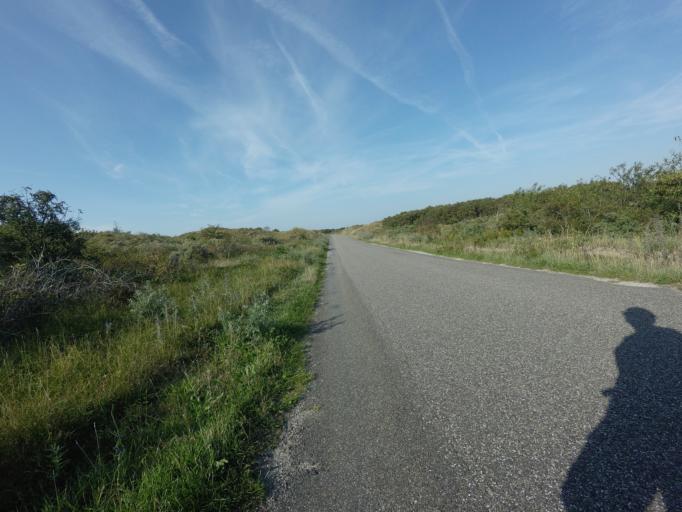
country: NL
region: Friesland
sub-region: Gemeente Schiermonnikoog
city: Schiermonnikoog
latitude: 53.4902
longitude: 6.1831
